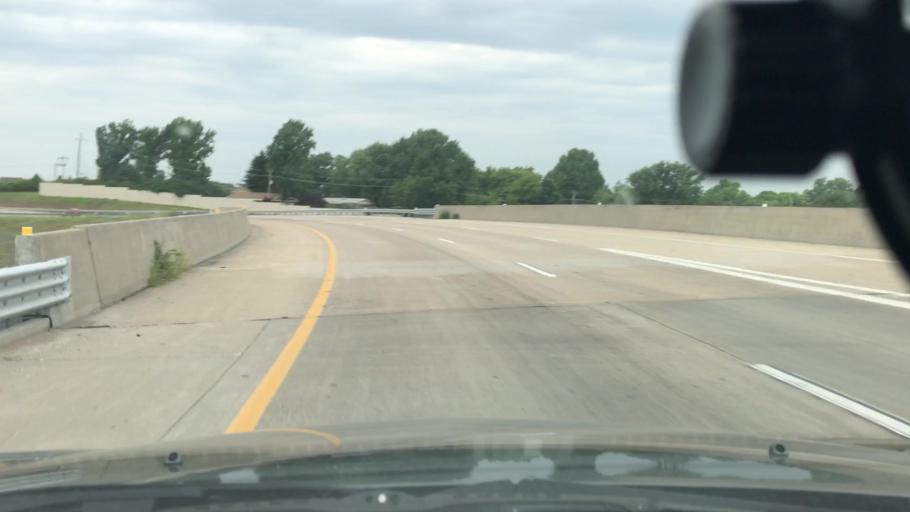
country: US
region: Missouri
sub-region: Saint Louis County
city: Maryland Heights
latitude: 38.7003
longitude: -90.4501
